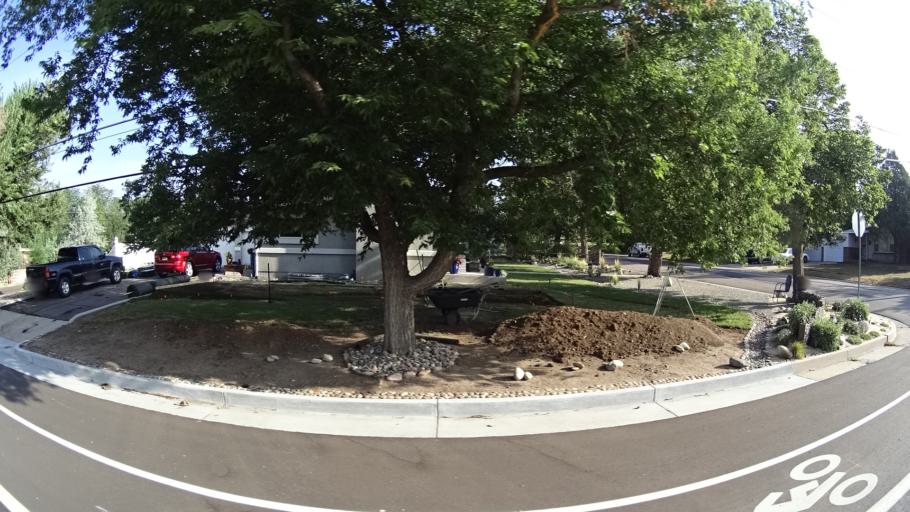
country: US
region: Colorado
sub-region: El Paso County
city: Colorado Springs
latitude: 38.8896
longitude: -104.8099
